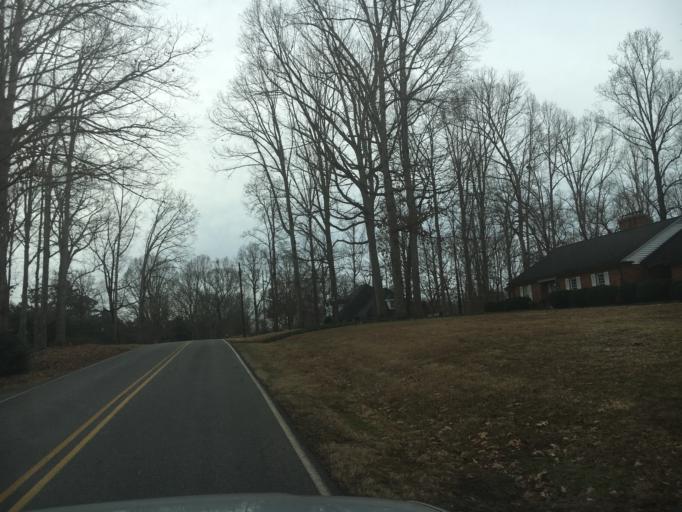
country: US
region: North Carolina
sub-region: Iredell County
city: Statesville
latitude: 35.7962
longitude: -80.8164
